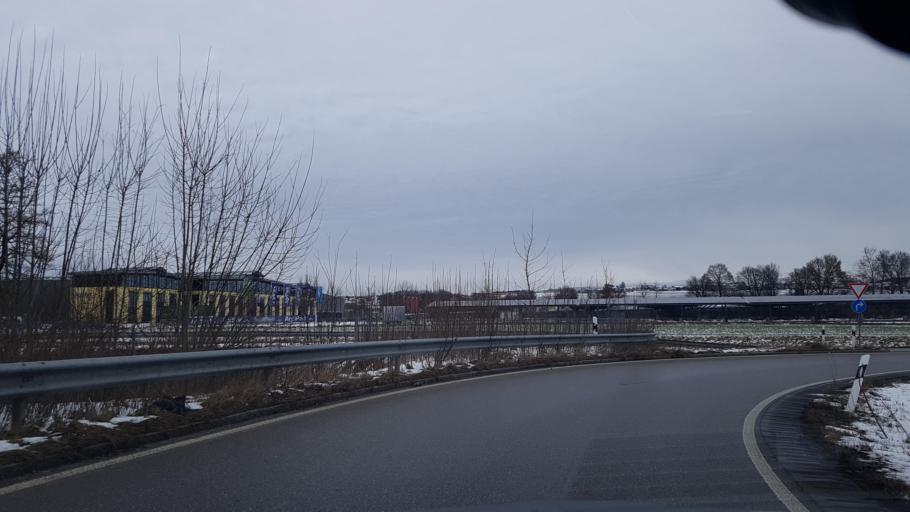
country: DE
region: Bavaria
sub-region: Upper Bavaria
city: Haag in Oberbayern
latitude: 48.1653
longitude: 12.1624
